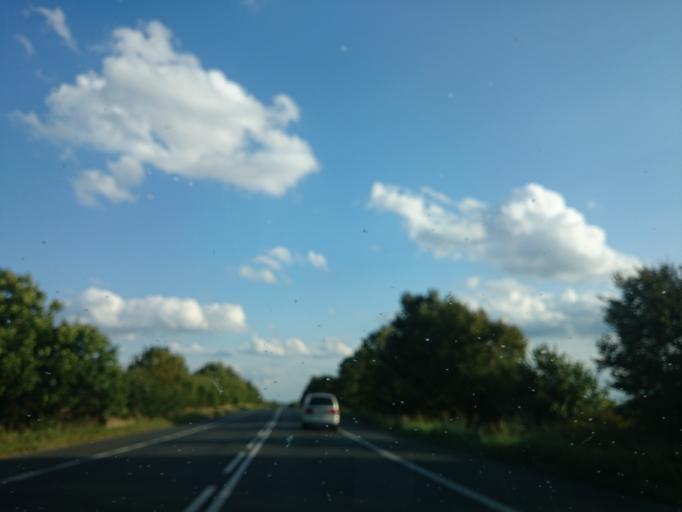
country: PL
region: West Pomeranian Voivodeship
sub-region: Powiat pyrzycki
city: Pyrzyce
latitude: 53.1182
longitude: 14.8922
